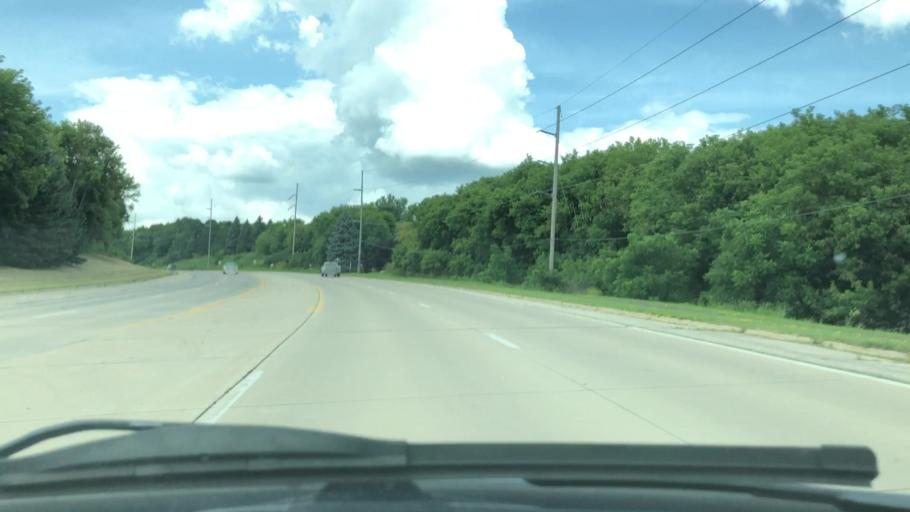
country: US
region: Minnesota
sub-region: Olmsted County
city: Rochester
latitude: 44.0096
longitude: -92.5091
